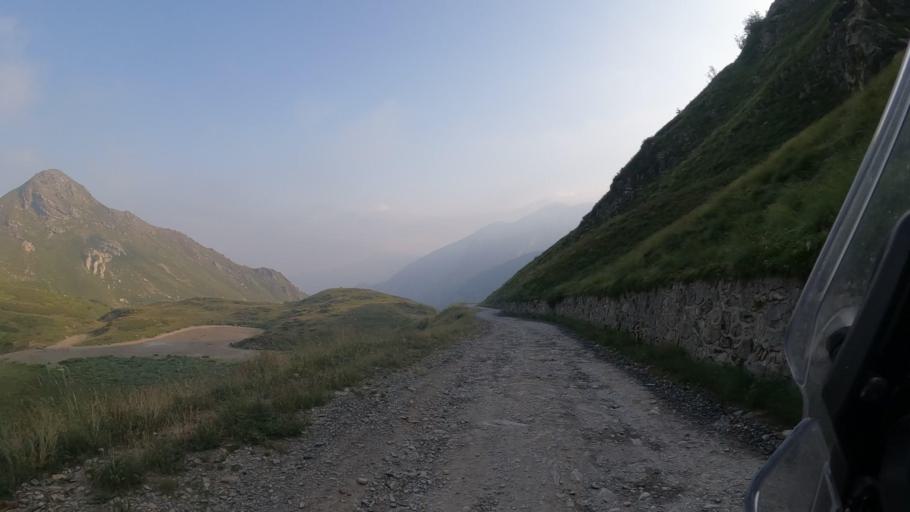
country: IT
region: Piedmont
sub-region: Provincia di Cuneo
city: Limone Piemonte
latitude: 44.1532
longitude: 7.6193
